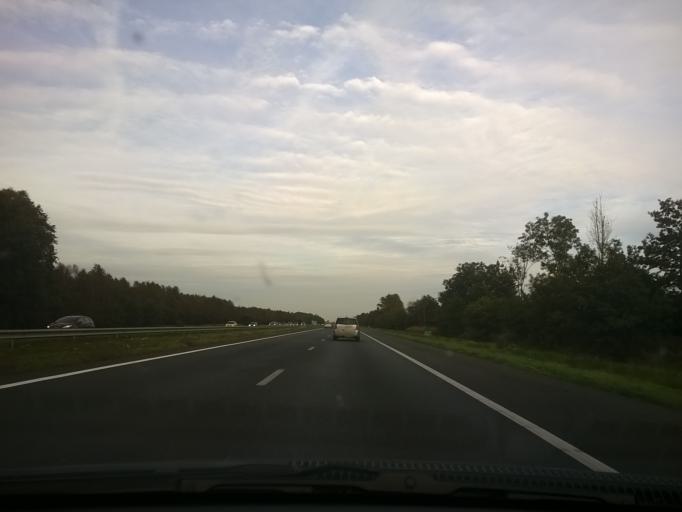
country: NL
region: Friesland
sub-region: Gemeente Achtkarspelen
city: Surhuisterveen
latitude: 53.1353
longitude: 6.2044
